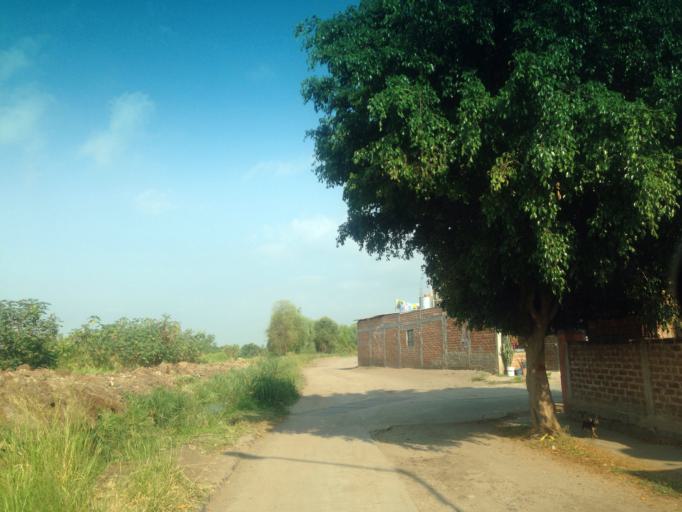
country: MX
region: Jalisco
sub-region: Atotonilco el Alto
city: Vistas del Maguey [Fraccionamiento]
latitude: 20.5272
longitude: -102.5298
